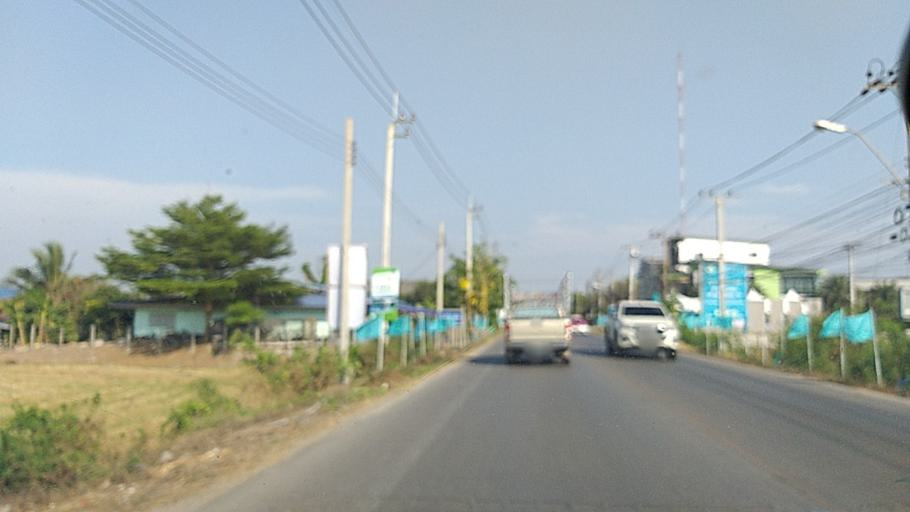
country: TH
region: Nonthaburi
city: Bang Bua Thong
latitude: 13.9374
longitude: 100.3667
